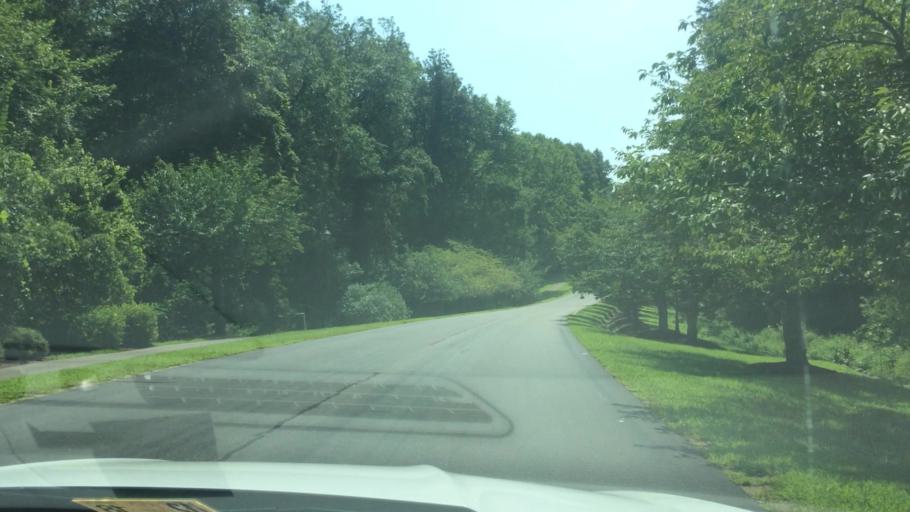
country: US
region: Virginia
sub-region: James City County
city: Williamsburg
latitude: 37.2987
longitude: -76.7706
